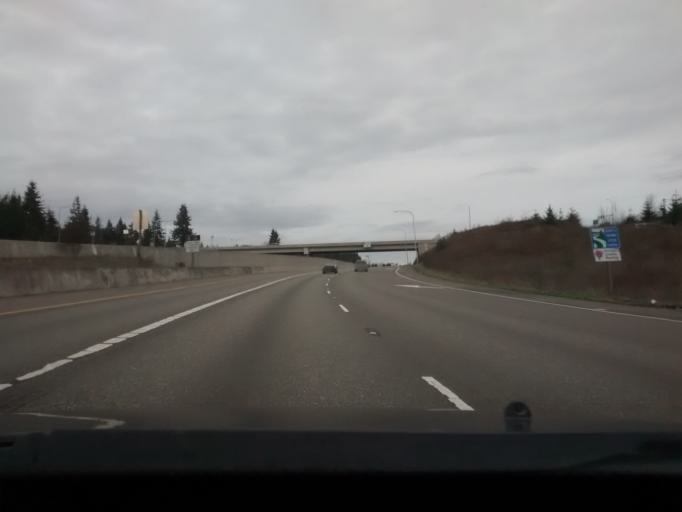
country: US
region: Washington
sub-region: Pierce County
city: Wollochet
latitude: 47.2774
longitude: -122.5605
